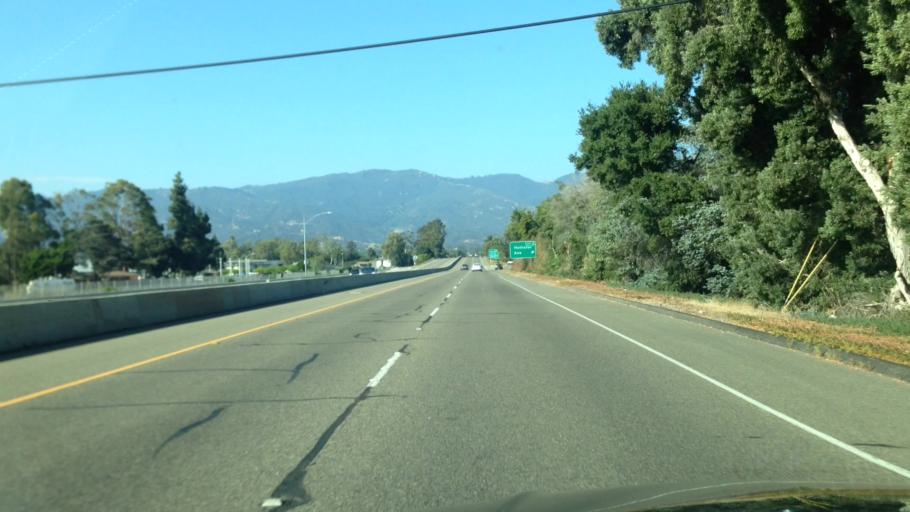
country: US
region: California
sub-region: Santa Barbara County
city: Goleta
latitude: 34.4301
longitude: -119.8220
